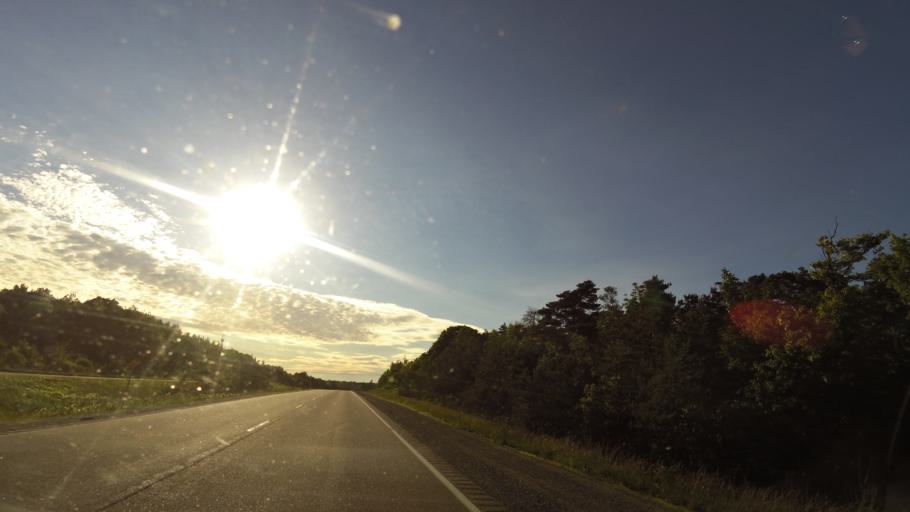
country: CA
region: Ontario
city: Midland
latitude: 44.7402
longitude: -79.6902
